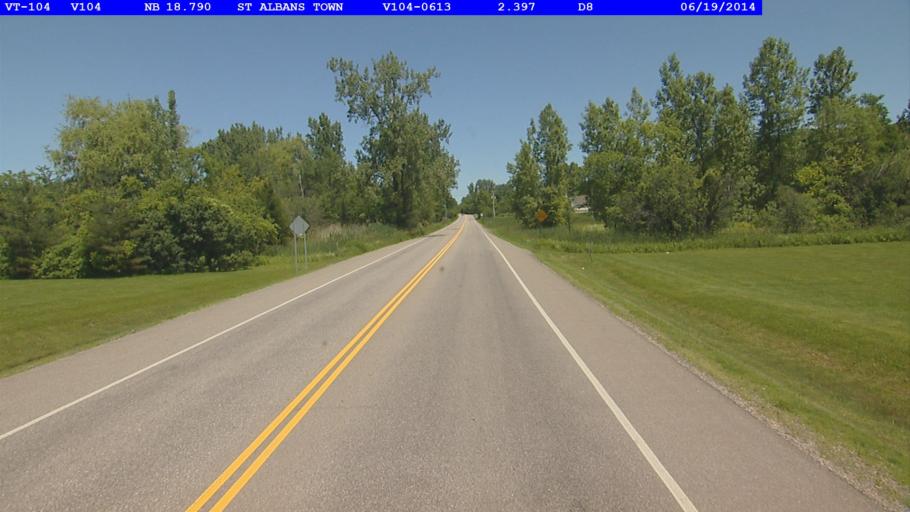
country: US
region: Vermont
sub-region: Franklin County
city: Saint Albans
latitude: 44.8070
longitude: -73.0675
